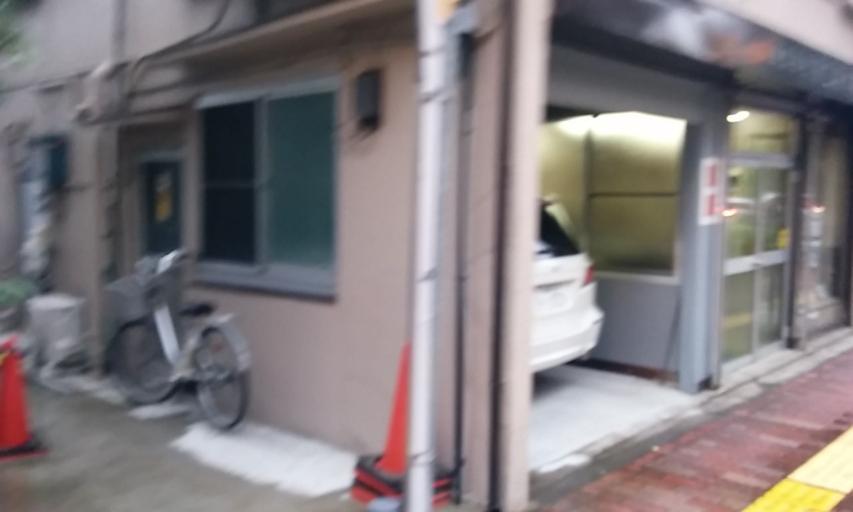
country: JP
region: Tokyo
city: Tokyo
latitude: 35.7024
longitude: 139.7648
